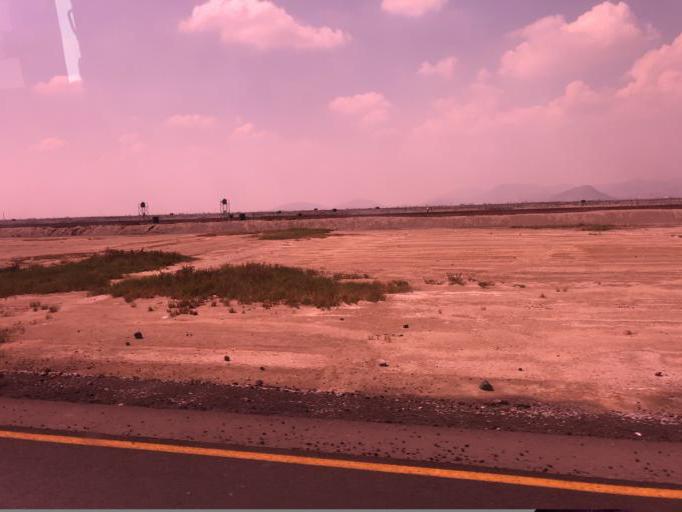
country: MX
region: Mexico
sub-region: Atenco
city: Colonia el Salado
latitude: 19.5349
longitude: -98.9853
